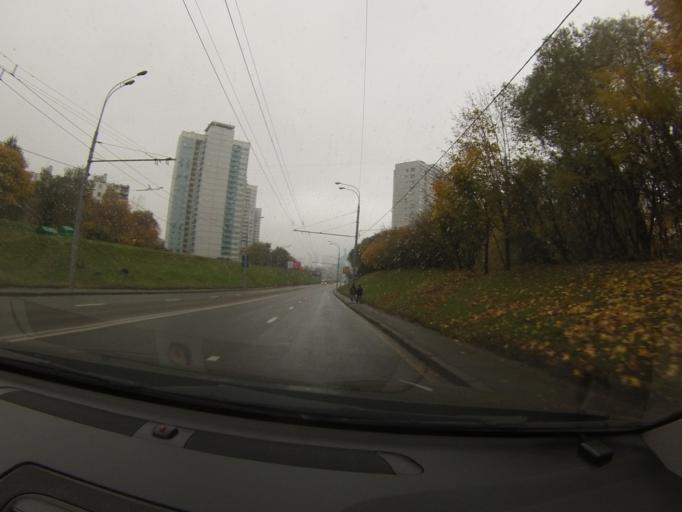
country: RU
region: Moscow
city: Troparevo
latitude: 55.6594
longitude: 37.4882
